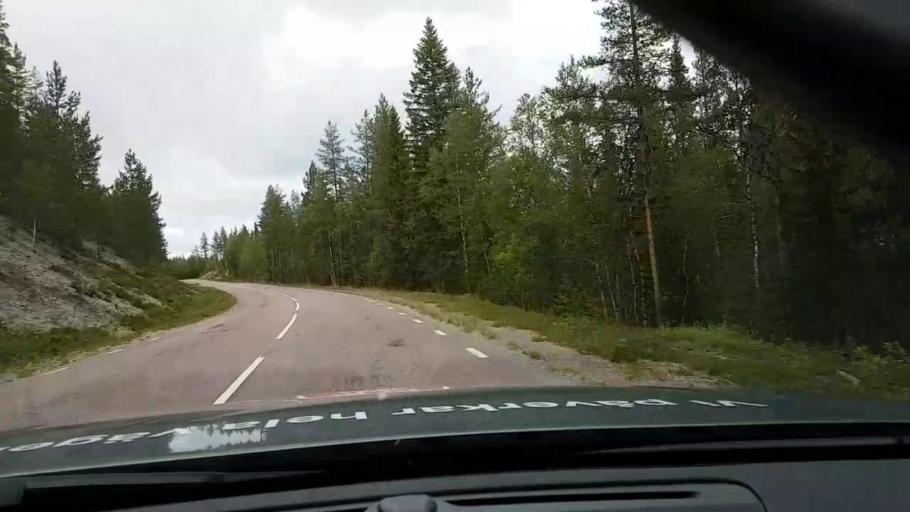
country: SE
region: Vaesterbotten
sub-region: Asele Kommun
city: Asele
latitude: 63.8758
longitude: 17.3567
